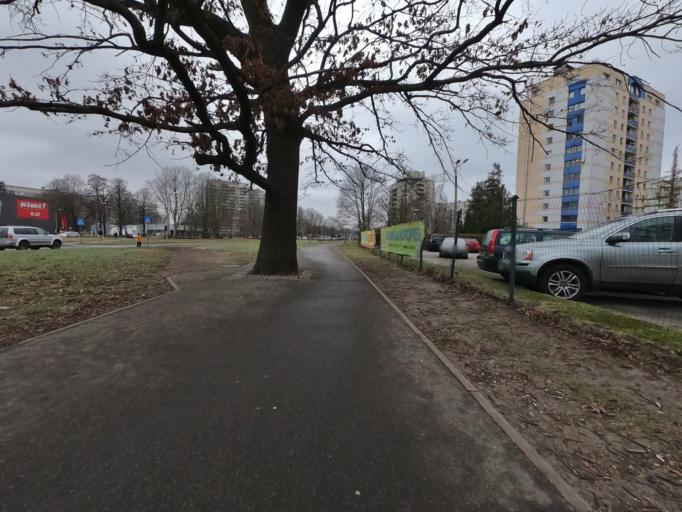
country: LV
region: Marupe
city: Marupe
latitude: 56.9448
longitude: 24.0147
